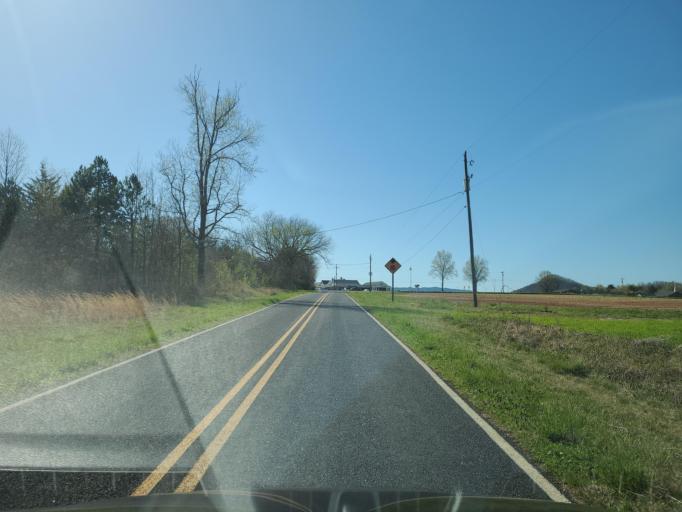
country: US
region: North Carolina
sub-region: Gaston County
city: Cherryville
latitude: 35.5303
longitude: -81.5084
